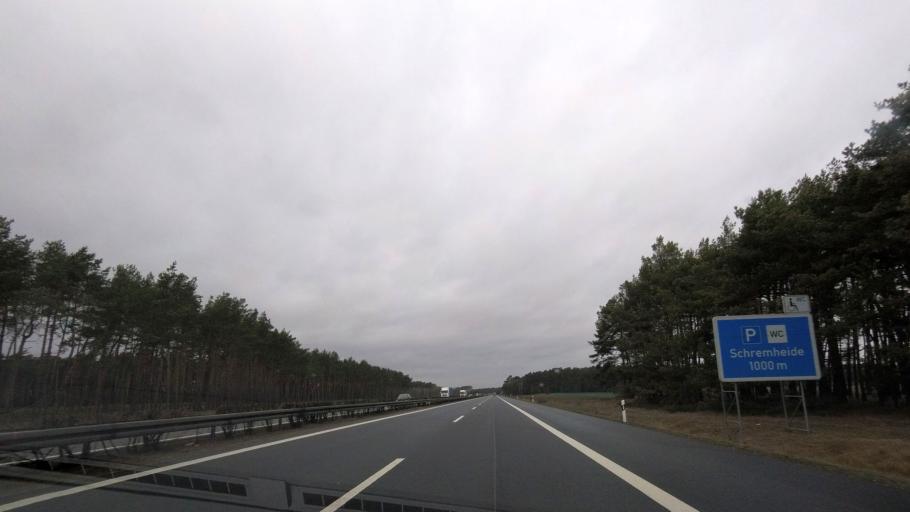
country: DE
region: Mecklenburg-Vorpommern
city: Sulstorf
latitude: 53.4536
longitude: 11.3584
